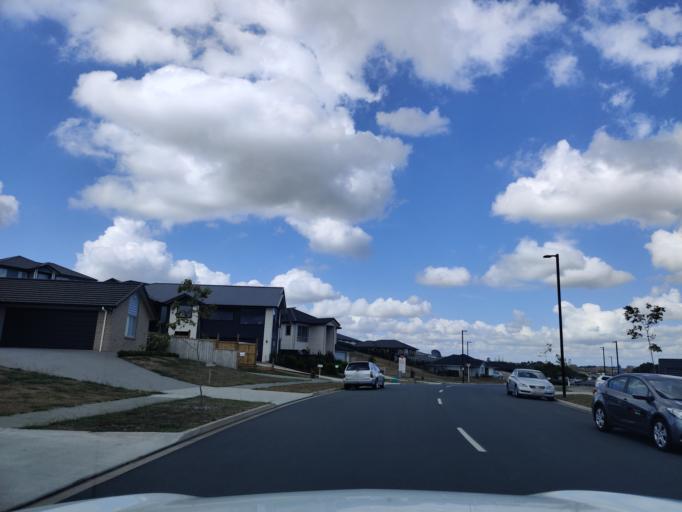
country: NZ
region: Auckland
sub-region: Auckland
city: Pukekohe East
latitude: -37.2378
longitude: 175.0178
